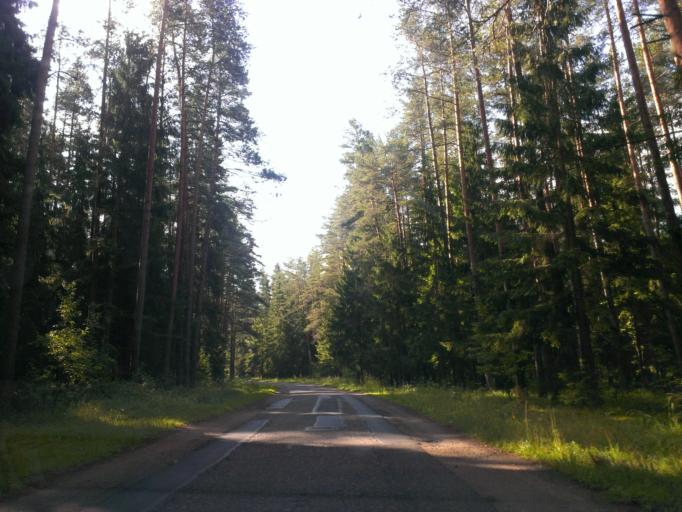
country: LV
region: Incukalns
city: Vangazi
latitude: 57.0973
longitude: 24.5347
